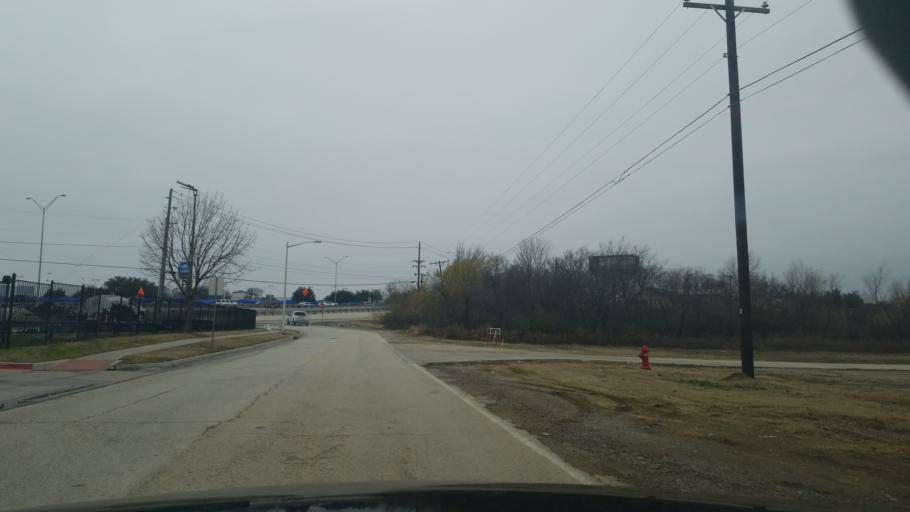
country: US
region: Texas
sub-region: Denton County
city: Corinth
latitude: 33.1713
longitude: -97.0851
